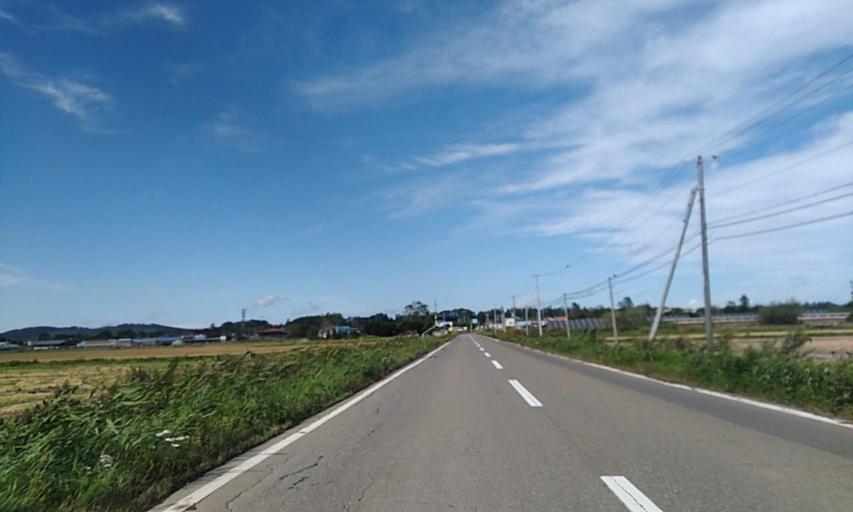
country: JP
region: Hokkaido
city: Obihiro
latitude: 42.7669
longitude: 143.6143
